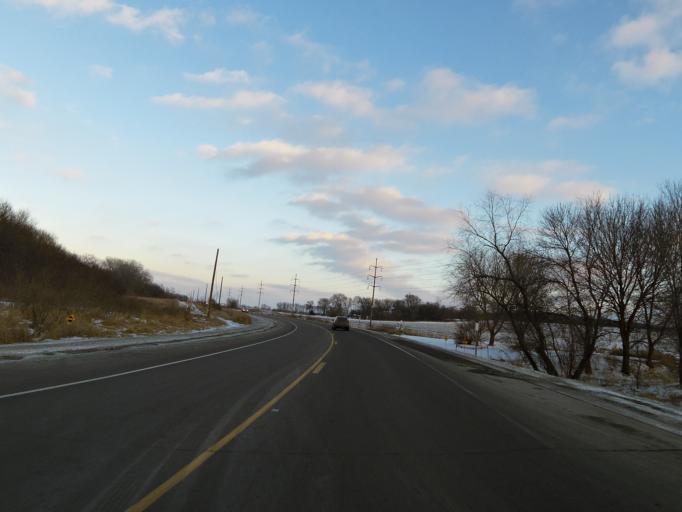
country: US
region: Minnesota
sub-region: Dakota County
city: Lakeville
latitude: 44.6384
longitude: -93.2777
